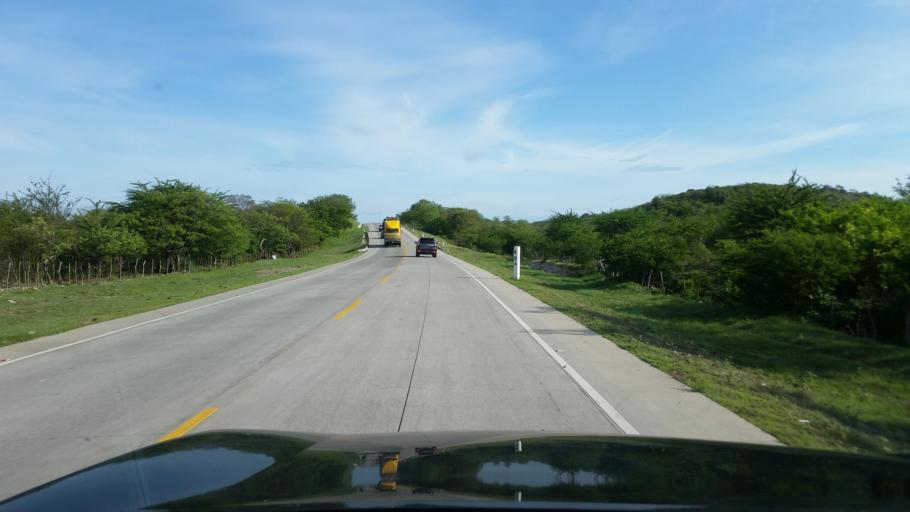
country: NI
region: Leon
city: Nagarote
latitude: 12.1767
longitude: -86.6678
